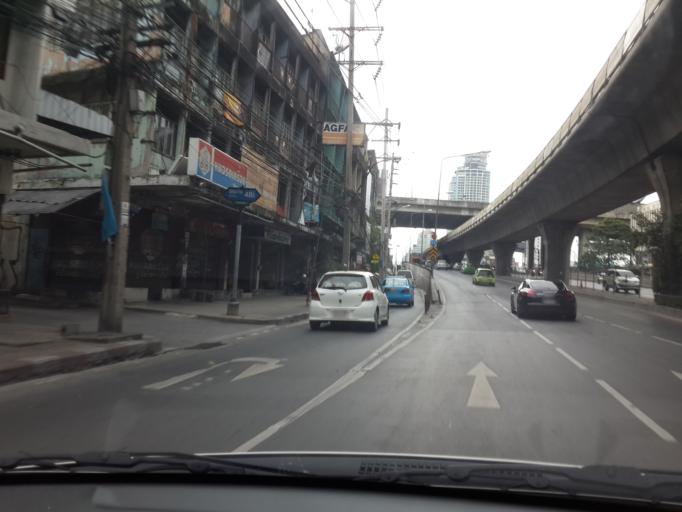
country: TH
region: Bangkok
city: Phra Khanong
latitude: 13.7095
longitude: 100.5988
